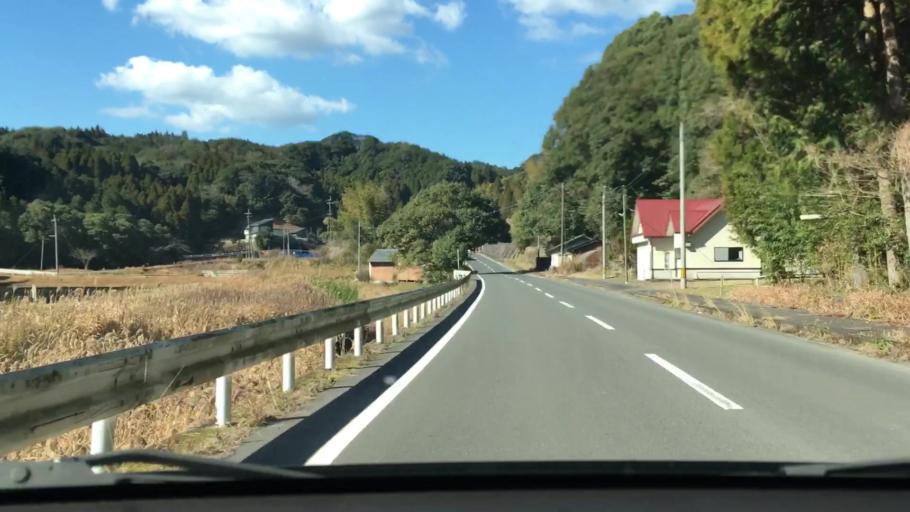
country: JP
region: Kagoshima
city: Ijuin
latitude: 31.6985
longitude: 130.4599
